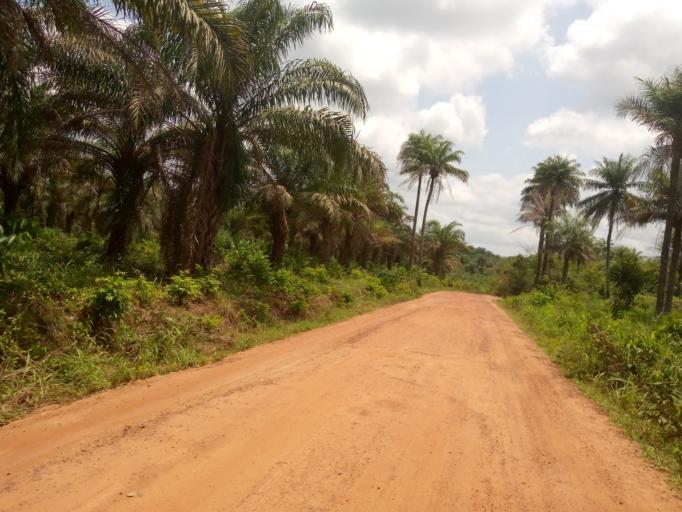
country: SL
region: Western Area
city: Waterloo
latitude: 8.3744
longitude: -12.9642
